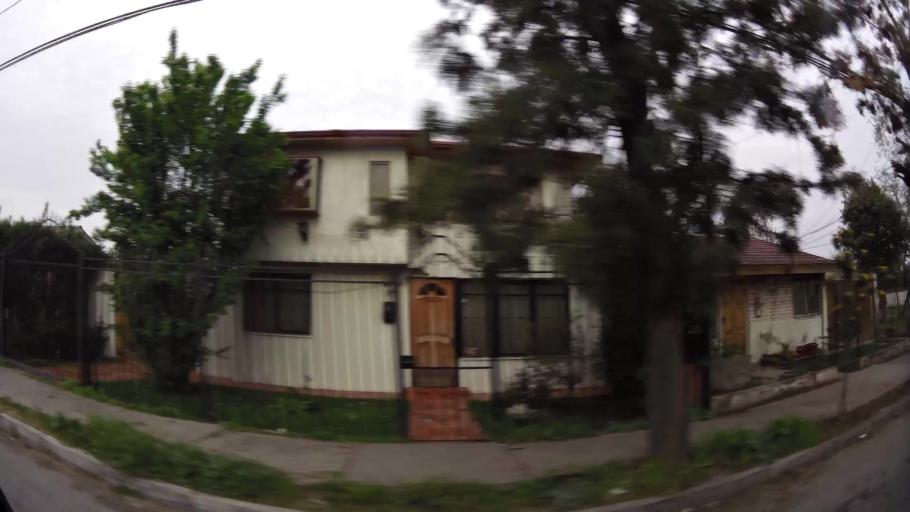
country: CL
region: Santiago Metropolitan
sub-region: Provincia de Santiago
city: Lo Prado
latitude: -33.5136
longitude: -70.7710
